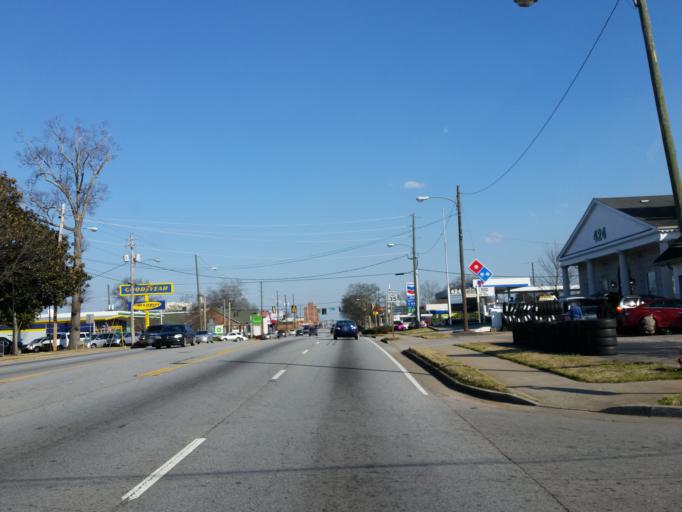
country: US
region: Georgia
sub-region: Spalding County
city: Griffin
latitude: 33.2472
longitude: -84.2702
